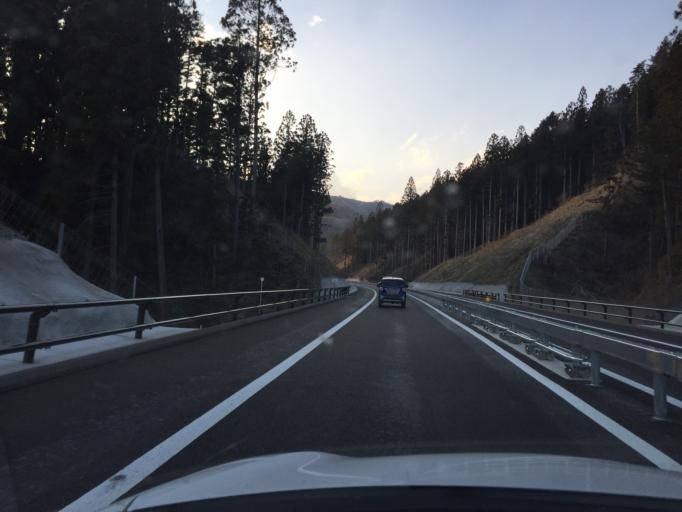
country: JP
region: Miyagi
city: Marumori
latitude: 37.7822
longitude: 140.8262
